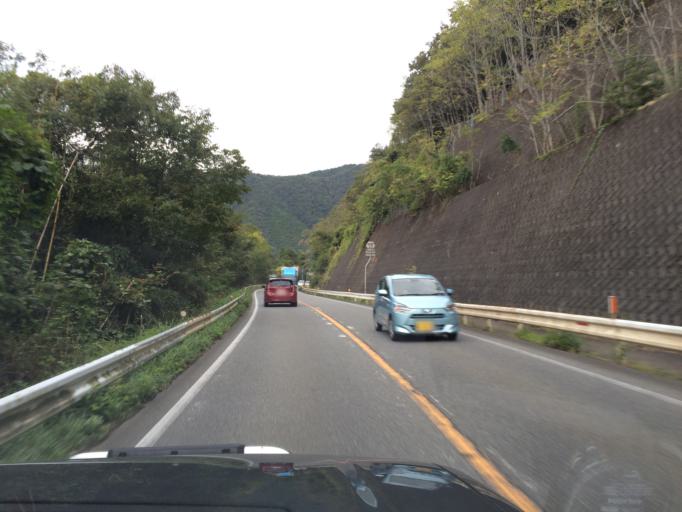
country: JP
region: Hyogo
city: Toyooka
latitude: 35.3691
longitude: 134.8204
